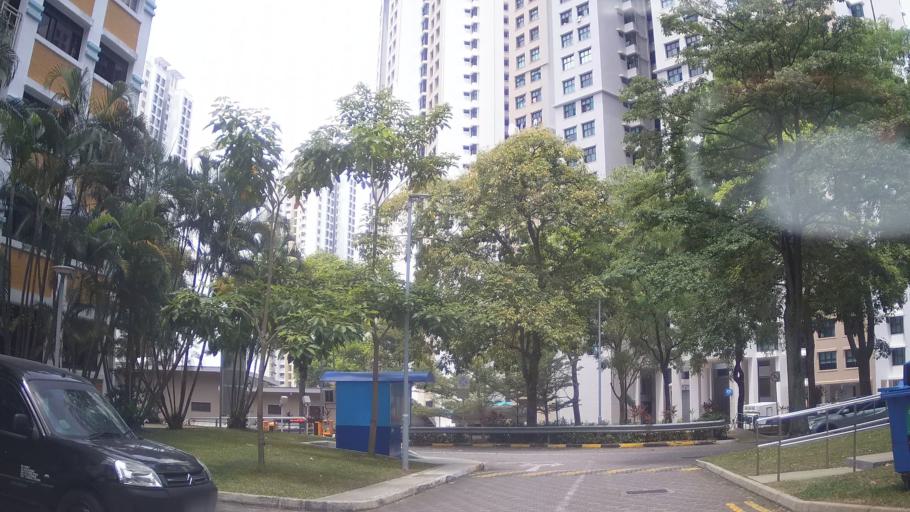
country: MY
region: Johor
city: Johor Bahru
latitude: 1.3852
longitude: 103.7612
